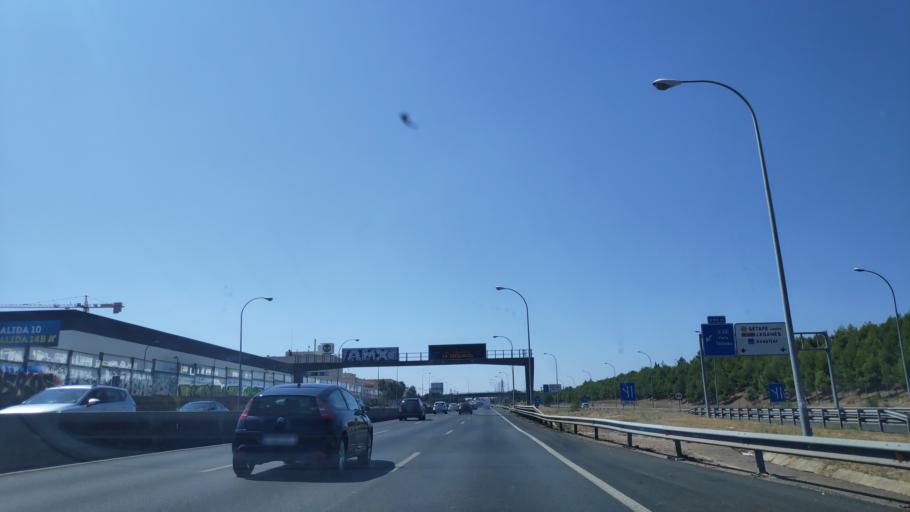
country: ES
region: Madrid
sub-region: Provincia de Madrid
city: Getafe
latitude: 40.3191
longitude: -3.7338
